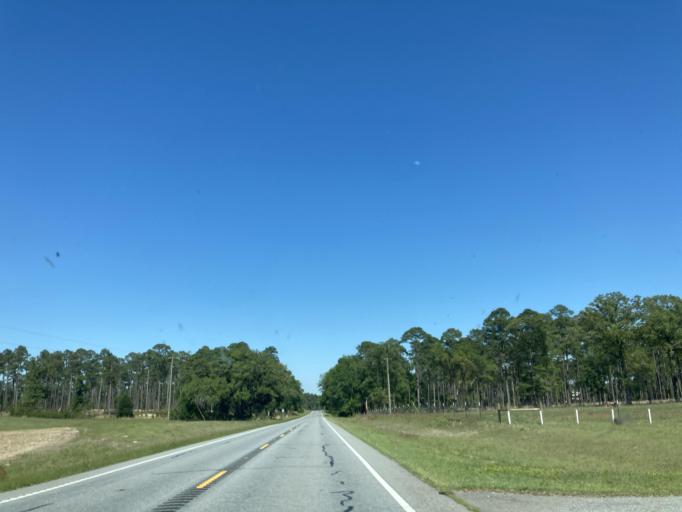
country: US
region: Georgia
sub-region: Baker County
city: Newton
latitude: 31.2100
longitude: -84.4871
